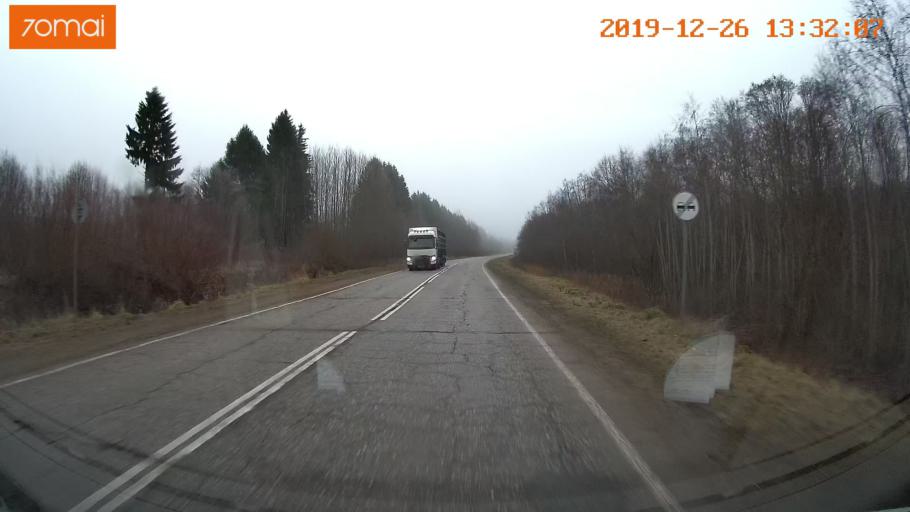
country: RU
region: Vologda
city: Sheksna
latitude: 58.8321
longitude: 38.2842
